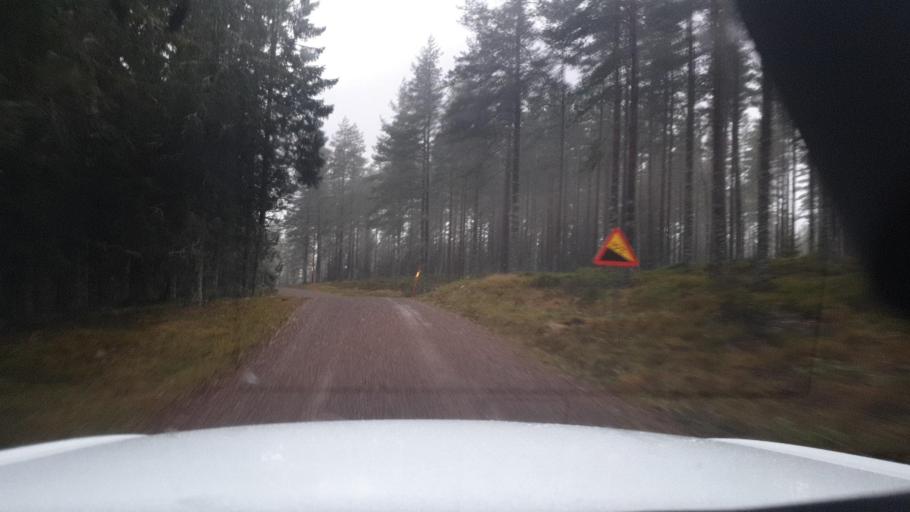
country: SE
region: Vaermland
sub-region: Torsby Kommun
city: Torsby
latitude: 59.9491
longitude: 12.7882
